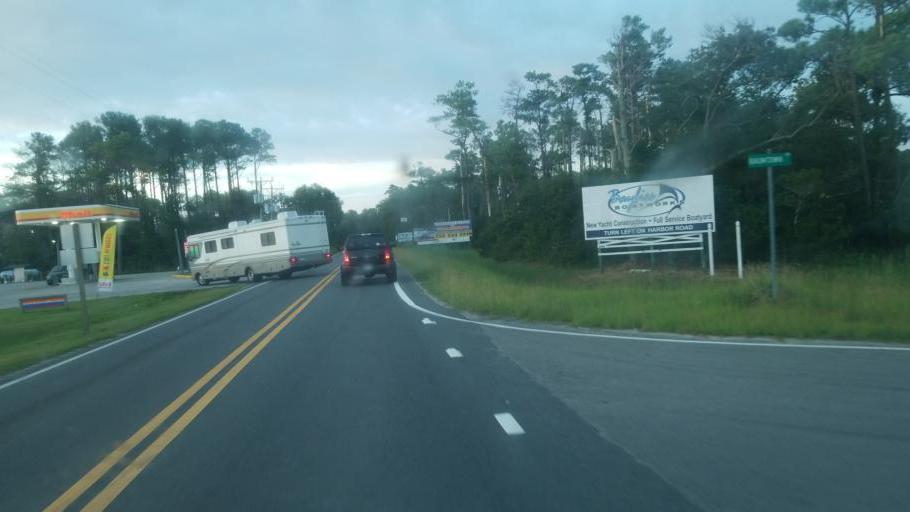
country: US
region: North Carolina
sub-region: Dare County
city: Wanchese
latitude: 35.8526
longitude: -75.6439
